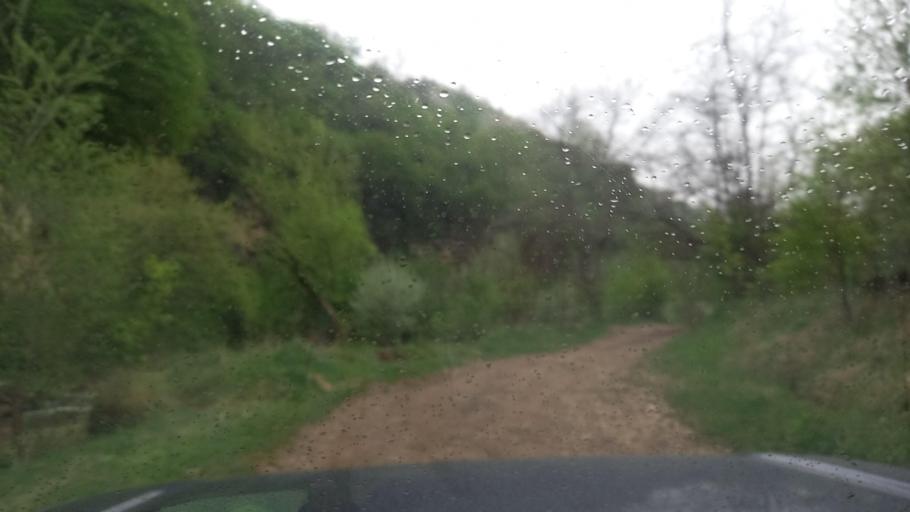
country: RU
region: Stavropol'skiy
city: Kislovodsk
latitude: 43.8875
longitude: 42.7041
